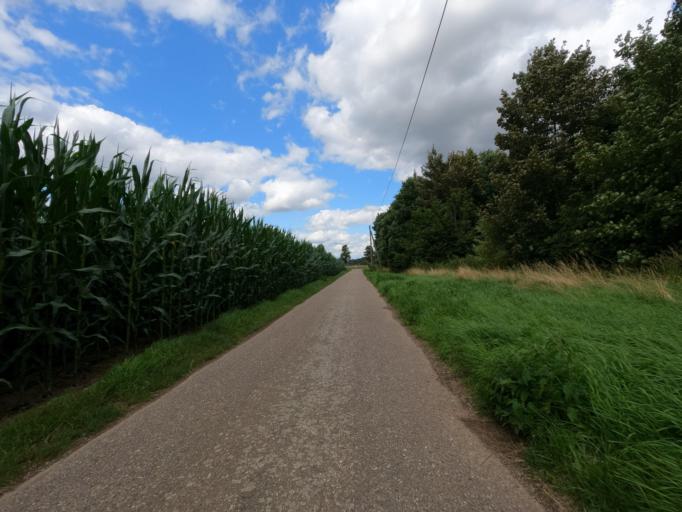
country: DE
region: North Rhine-Westphalia
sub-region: Regierungsbezirk Koln
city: Linnich
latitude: 50.9951
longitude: 6.2705
